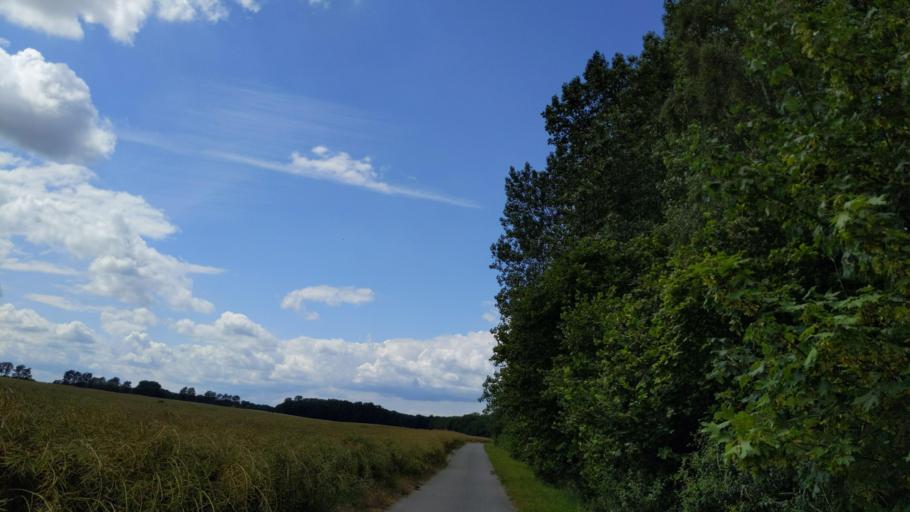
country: DE
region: Mecklenburg-Vorpommern
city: Klutz
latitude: 54.0103
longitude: 11.1210
